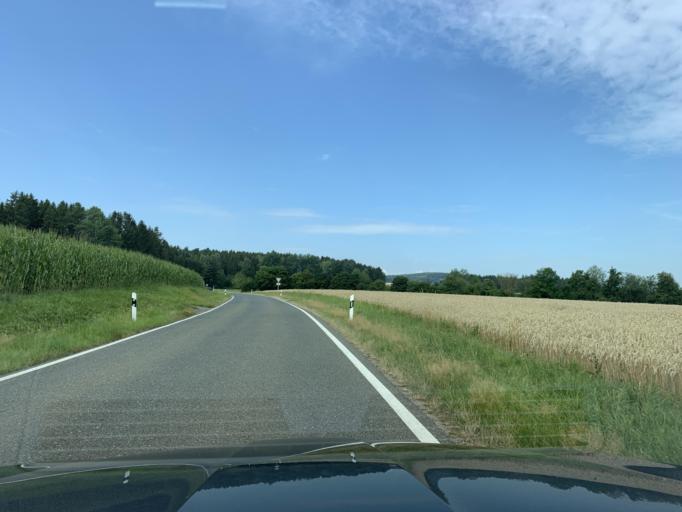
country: DE
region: Bavaria
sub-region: Upper Palatinate
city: Winklarn
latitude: 49.4100
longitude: 12.4992
